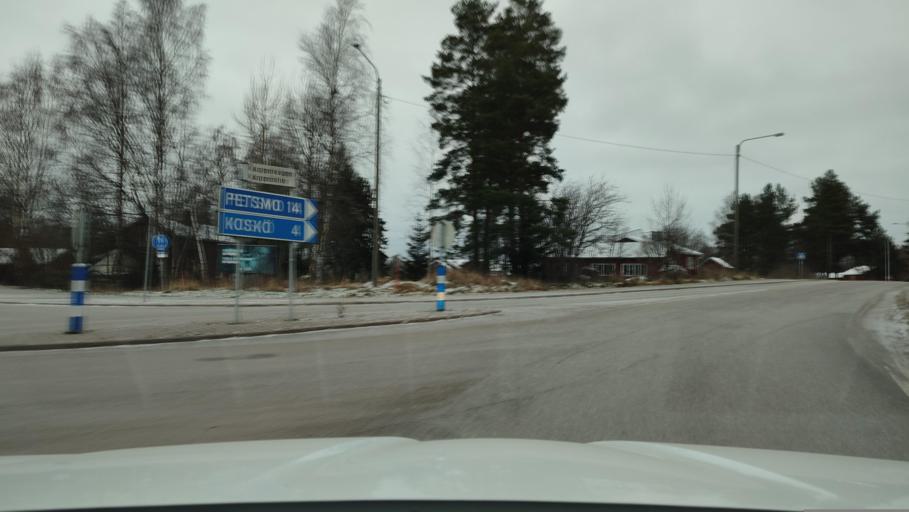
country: FI
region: Ostrobothnia
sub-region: Vaasa
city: Smedsby
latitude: 63.1543
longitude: 21.6918
